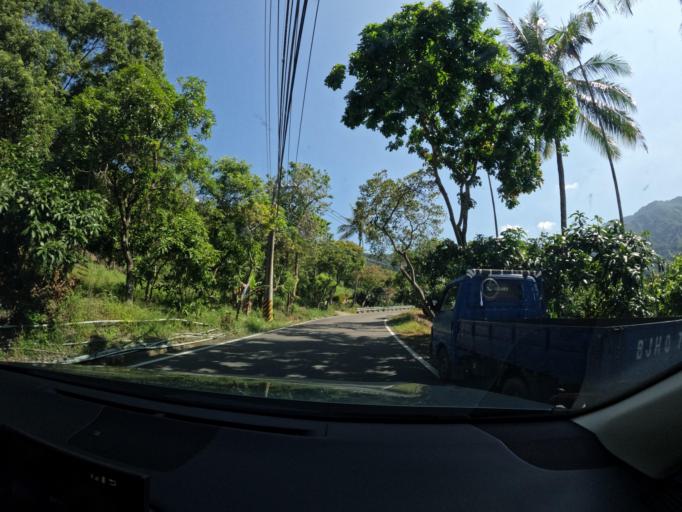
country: TW
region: Taiwan
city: Yujing
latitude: 23.1352
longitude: 120.7238
